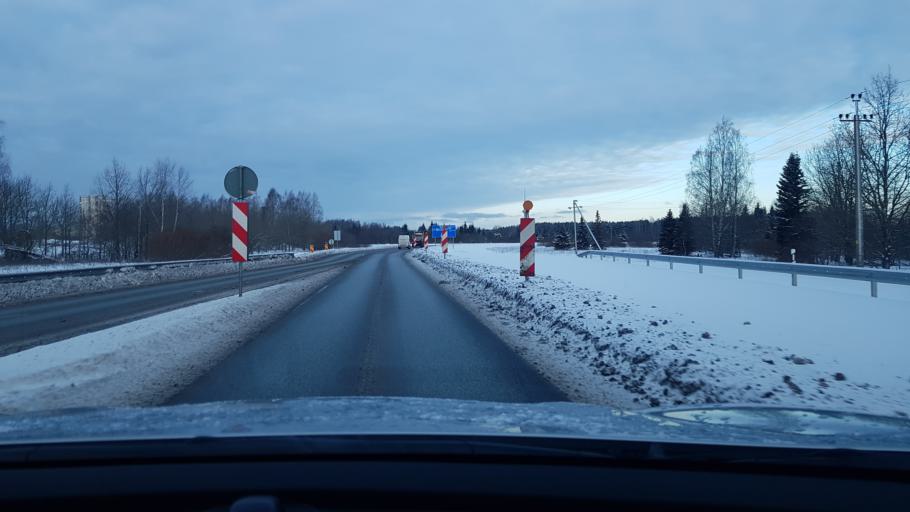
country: EE
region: Harju
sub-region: Joelaehtme vald
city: Loo
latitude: 59.4388
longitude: 24.9125
